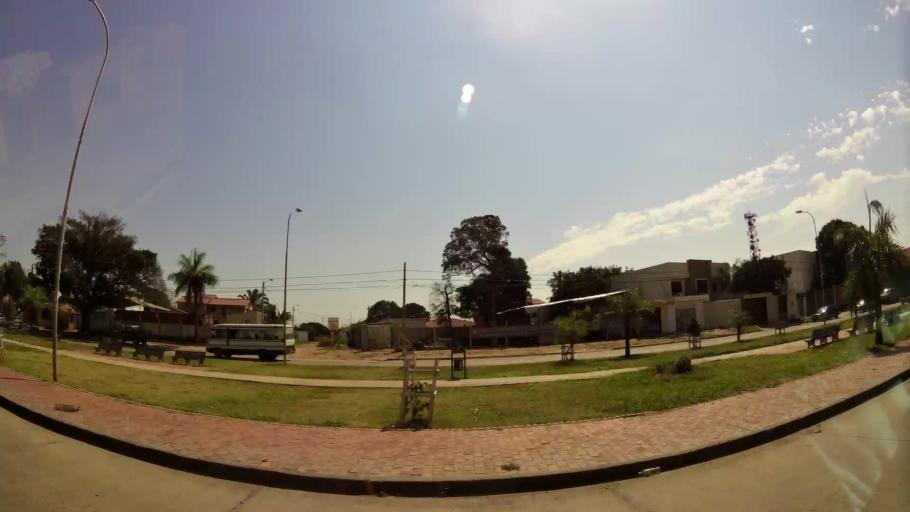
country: BO
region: Santa Cruz
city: Santa Cruz de la Sierra
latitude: -17.7391
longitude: -63.1559
